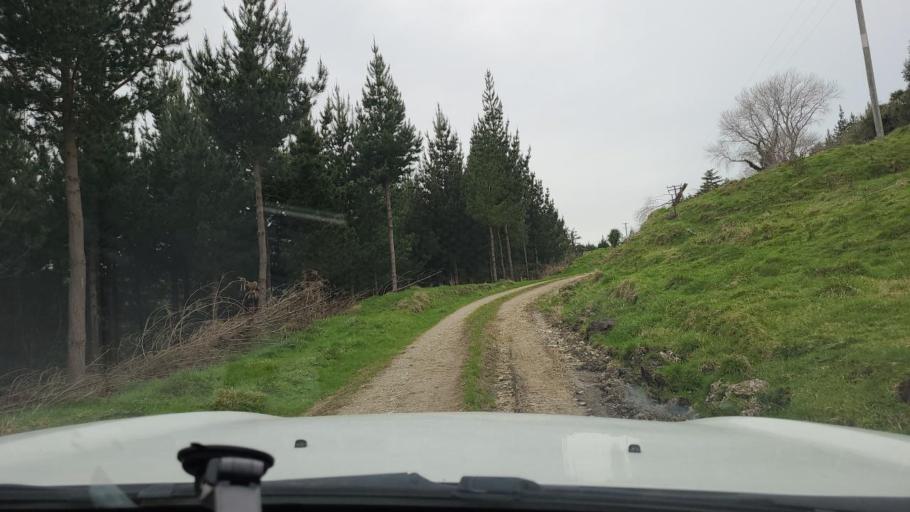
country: NZ
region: Gisborne
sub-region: Gisborne District
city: Gisborne
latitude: -38.5189
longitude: 178.0927
